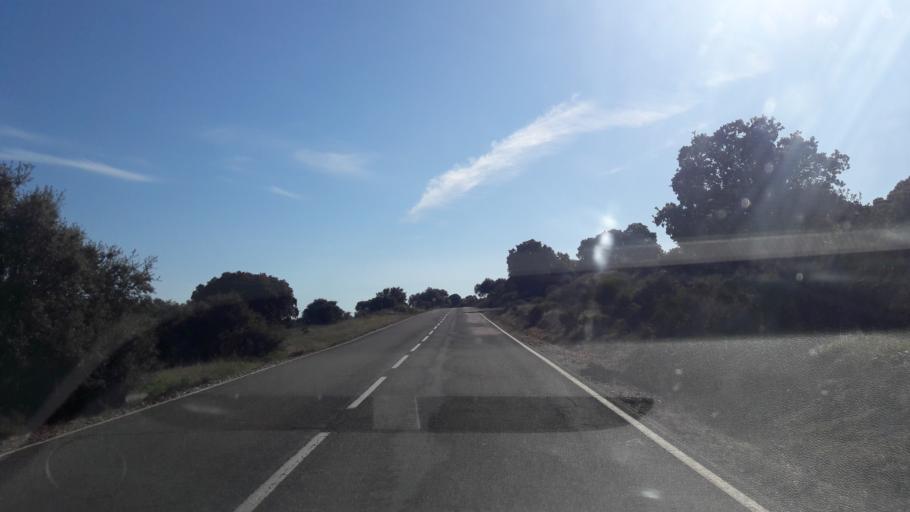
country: ES
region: Castille and Leon
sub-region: Provincia de Avila
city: Narrillos del Alamo
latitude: 40.5315
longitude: -5.4755
